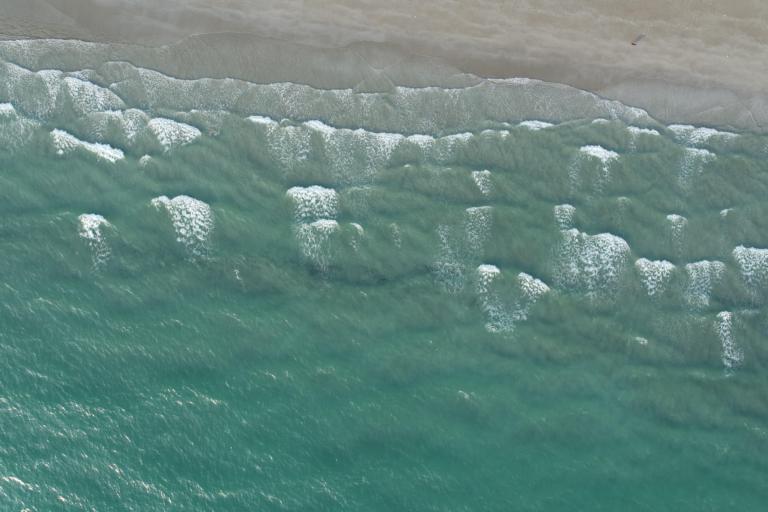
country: TH
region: Rayong
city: Rayong
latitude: 12.5971
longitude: 101.4073
